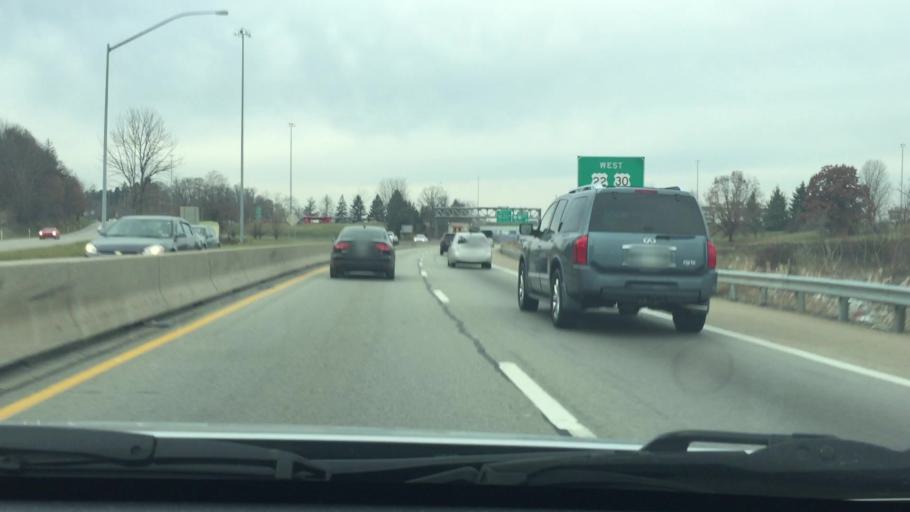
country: US
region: Pennsylvania
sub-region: Allegheny County
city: Oakdale
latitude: 40.4449
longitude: -80.1639
